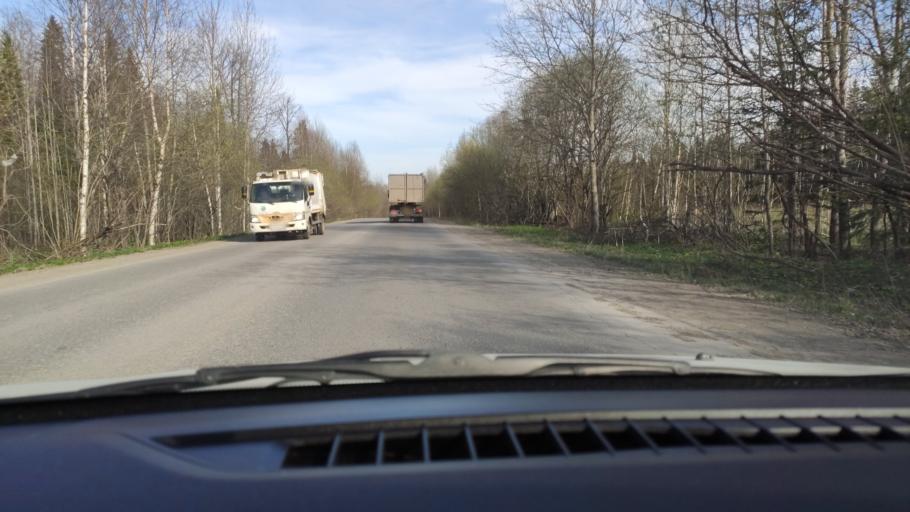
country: RU
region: Perm
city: Ferma
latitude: 57.9397
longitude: 56.4487
